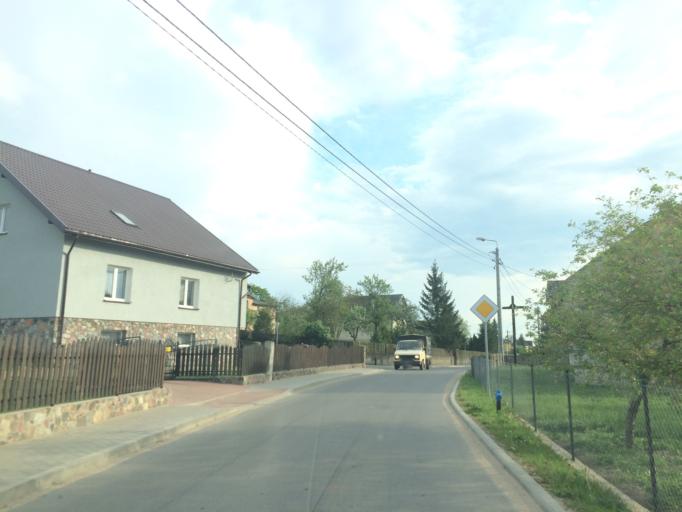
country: PL
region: Kujawsko-Pomorskie
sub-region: Powiat brodnicki
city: Brzozie
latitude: 53.3585
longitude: 19.7096
